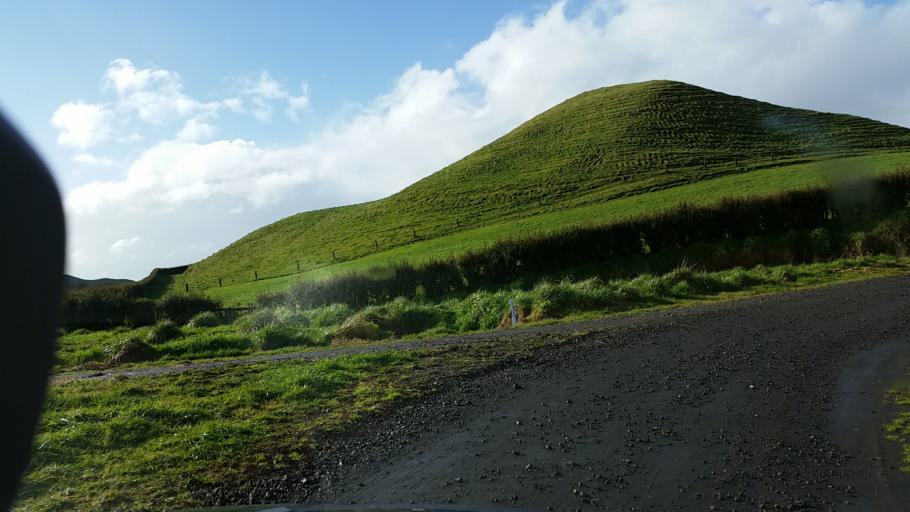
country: NZ
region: Taranaki
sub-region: South Taranaki District
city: Eltham
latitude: -39.3461
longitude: 174.4386
